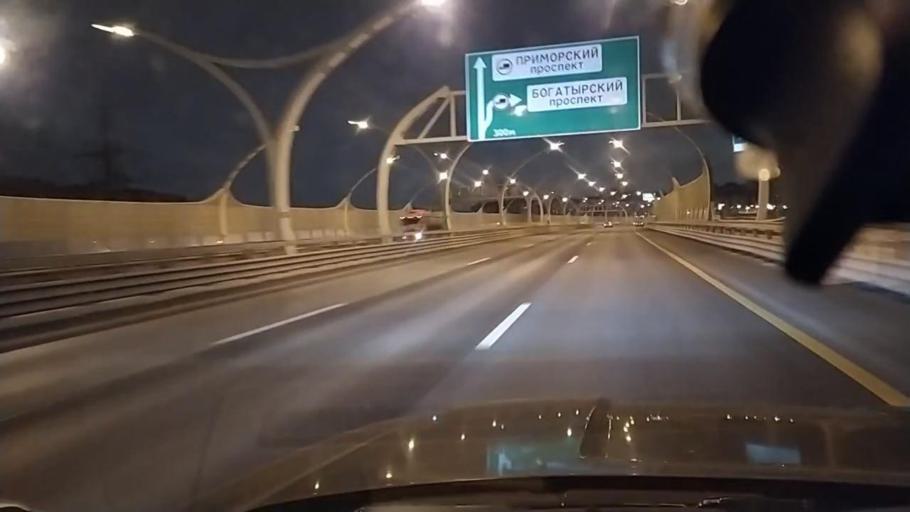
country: RU
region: Leningrad
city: Untolovo
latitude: 60.0117
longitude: 30.2309
